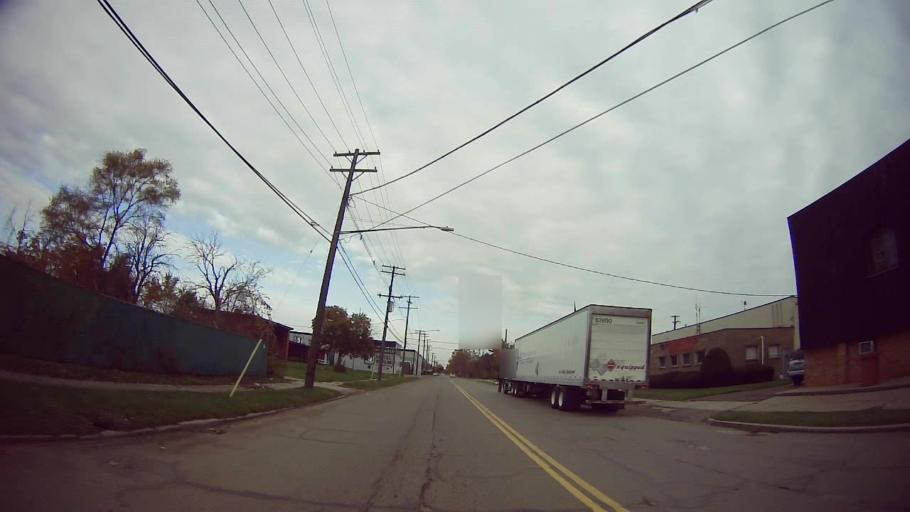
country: US
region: Michigan
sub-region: Wayne County
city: Dearborn
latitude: 42.3609
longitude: -83.1873
